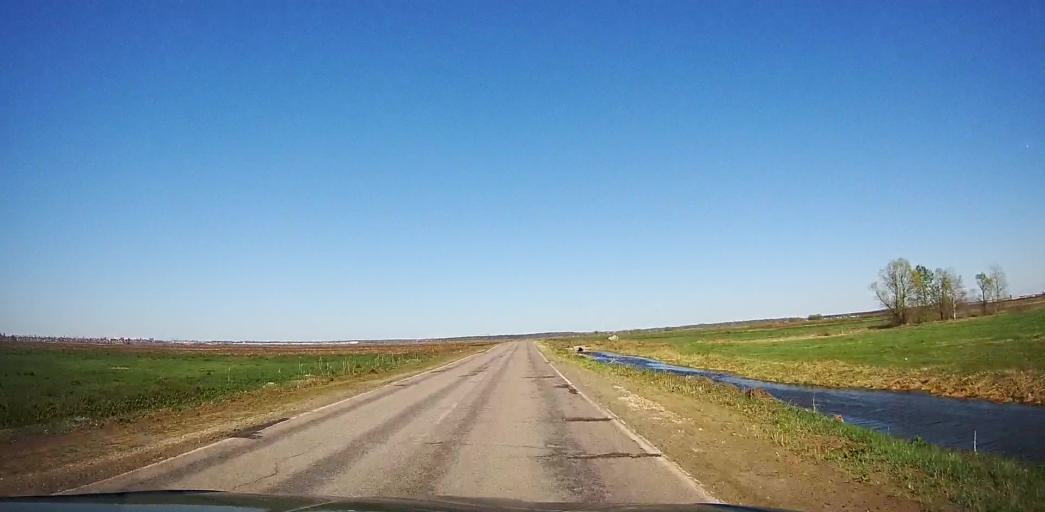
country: RU
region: Moskovskaya
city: Ramenskoye
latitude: 55.5048
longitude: 38.2500
